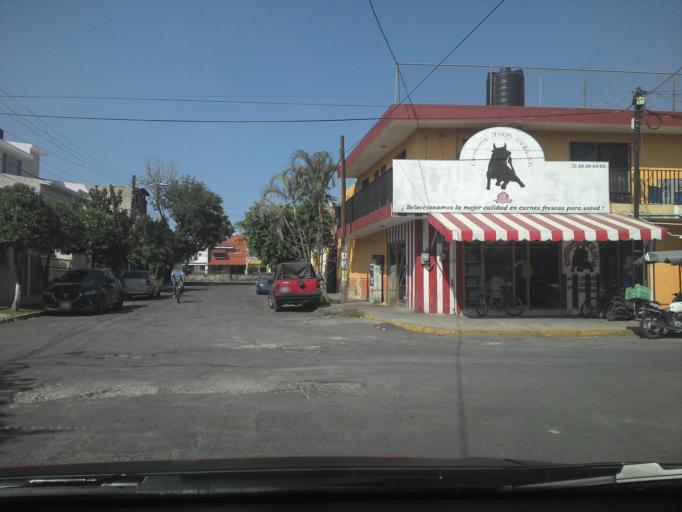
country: MX
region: Jalisco
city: Guadalajara
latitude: 20.6463
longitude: -103.4340
